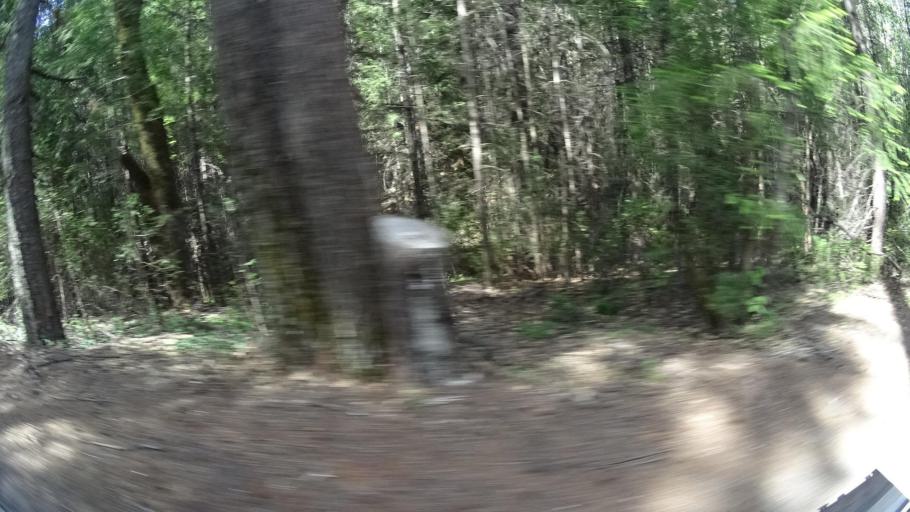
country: US
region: California
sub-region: Lake County
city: Cobb
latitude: 38.8714
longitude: -122.7224
